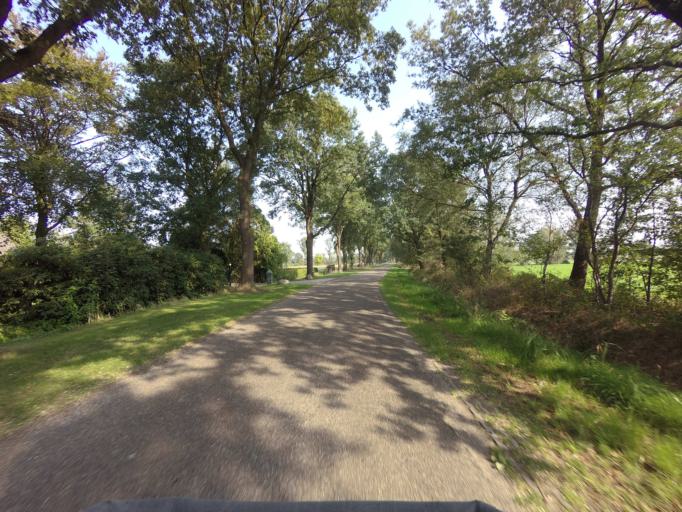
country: NL
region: Drenthe
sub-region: Gemeente Tynaarlo
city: Vries
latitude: 53.1302
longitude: 6.5270
